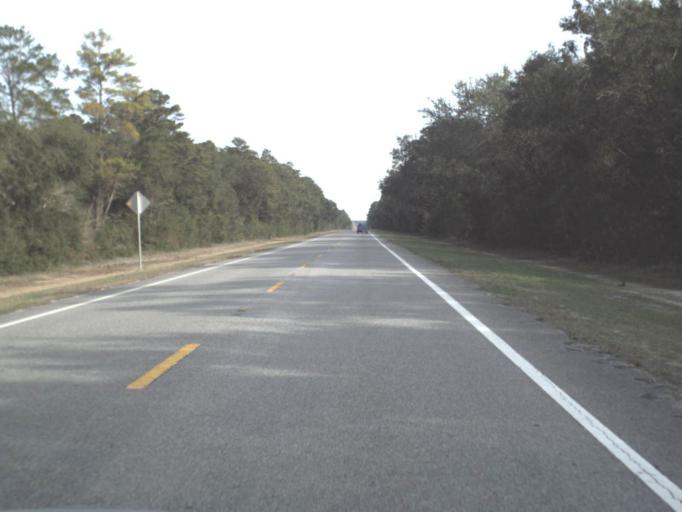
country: US
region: Florida
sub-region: Bay County
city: Mexico Beach
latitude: 29.9621
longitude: -85.4421
